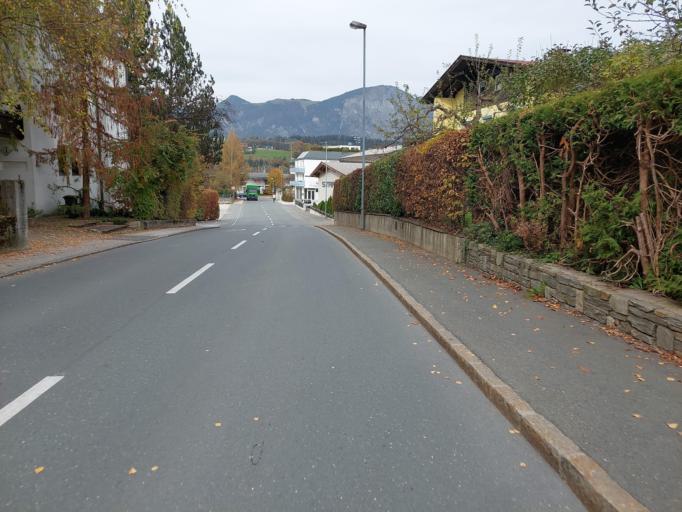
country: AT
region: Tyrol
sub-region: Politischer Bezirk Kufstein
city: Worgl
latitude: 47.4857
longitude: 12.0584
